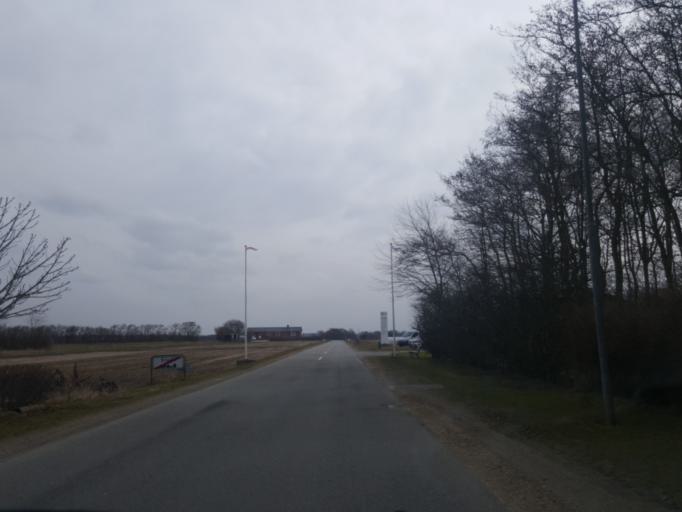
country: DK
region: Central Jutland
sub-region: Ringkobing-Skjern Kommune
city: Ringkobing
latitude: 56.1980
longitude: 8.2174
